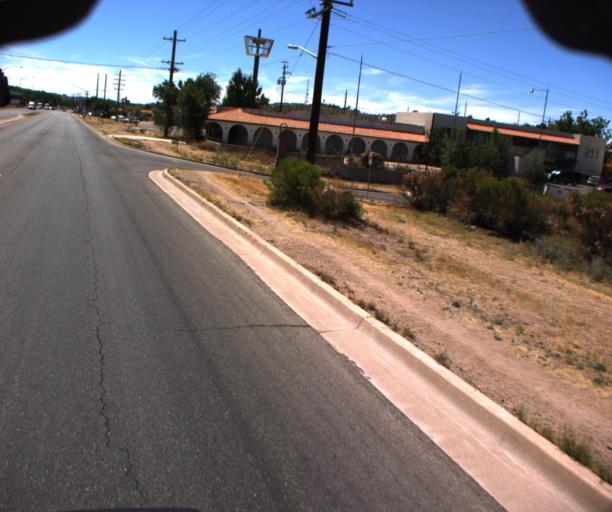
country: US
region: Arizona
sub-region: Santa Cruz County
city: Nogales
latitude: 31.3814
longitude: -110.9452
